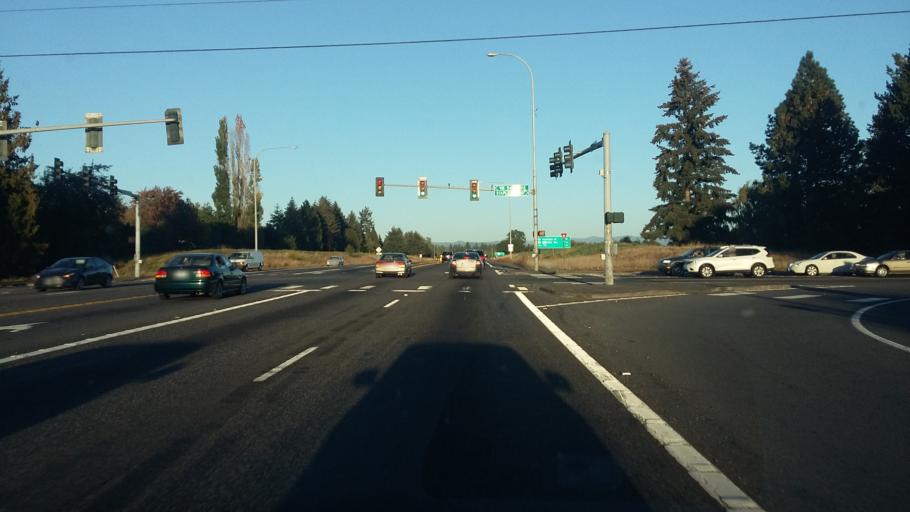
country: US
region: Washington
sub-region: Clark County
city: Walnut Grove
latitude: 45.6478
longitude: -122.6175
